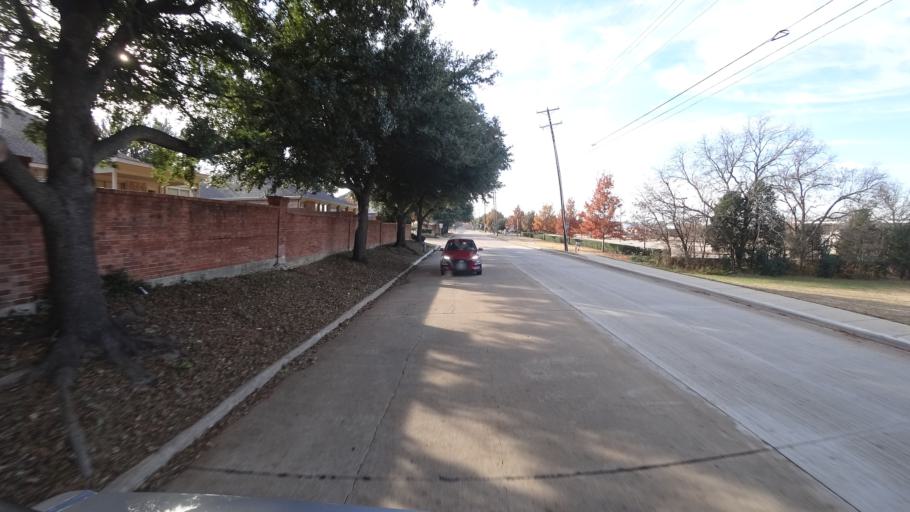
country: US
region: Texas
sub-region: Collin County
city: McKinney
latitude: 33.2016
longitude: -96.6547
